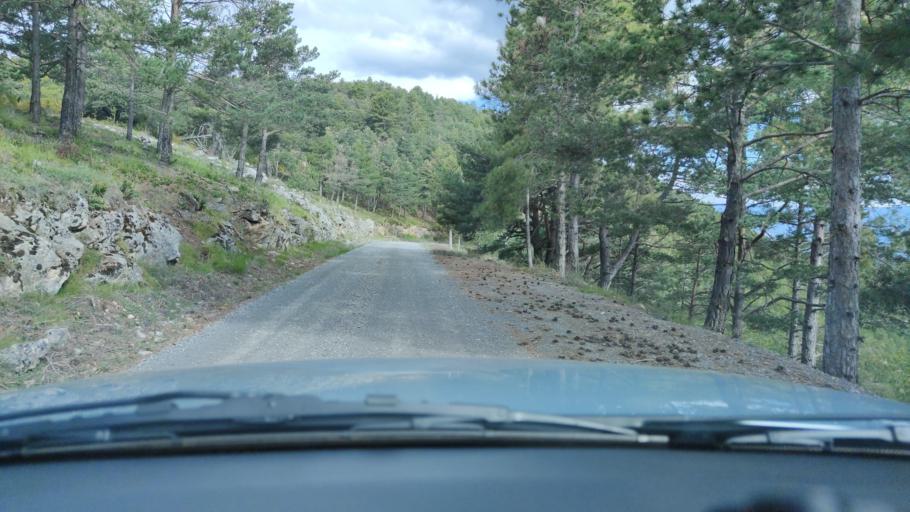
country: ES
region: Catalonia
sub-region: Provincia de Lleida
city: Coll de Nargo
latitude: 42.2436
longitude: 1.4099
